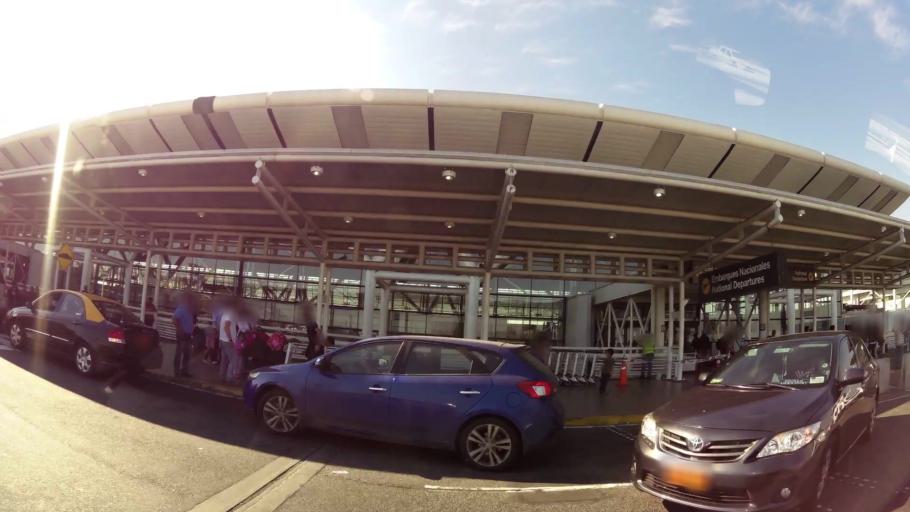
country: CL
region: Santiago Metropolitan
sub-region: Provincia de Santiago
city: Lo Prado
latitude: -33.3972
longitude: -70.7930
